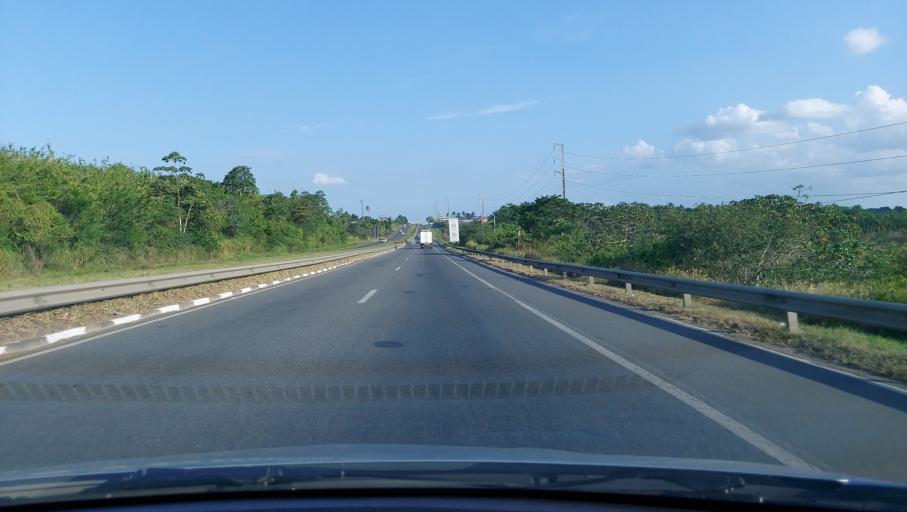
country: BR
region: Bahia
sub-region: Conceicao Do Jacuipe
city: Conceicao do Jacuipe
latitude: -12.3629
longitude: -38.8218
